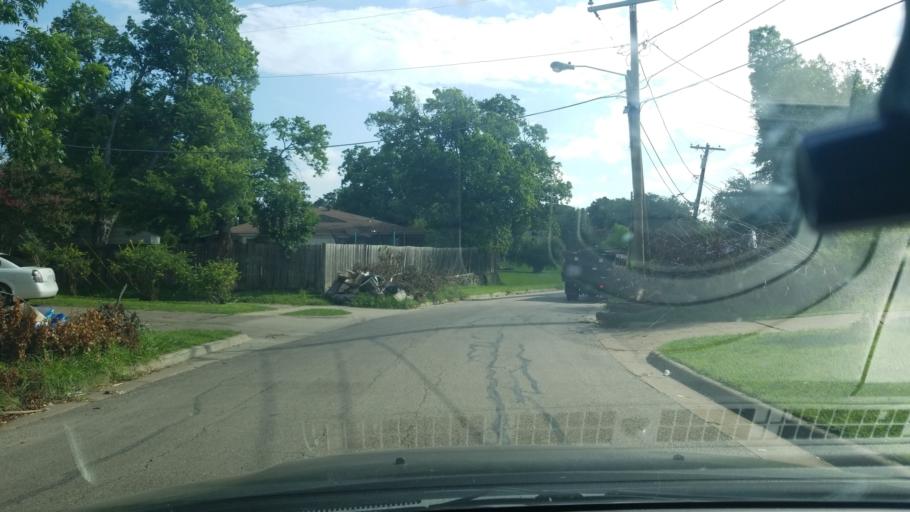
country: US
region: Texas
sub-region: Dallas County
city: Balch Springs
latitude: 32.7452
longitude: -96.6633
